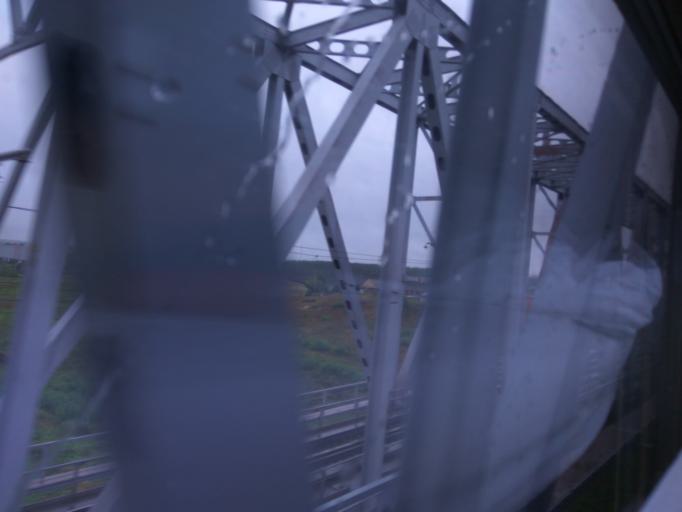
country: RU
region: Moskovskaya
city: Kashira
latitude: 54.8625
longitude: 38.1637
